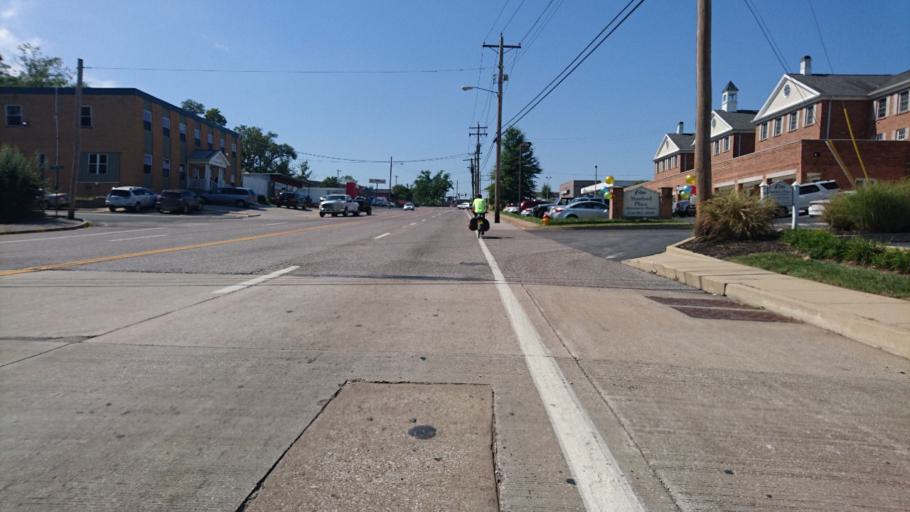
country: US
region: Missouri
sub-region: Saint Louis County
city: Brentwood
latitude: 38.6106
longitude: -90.3607
